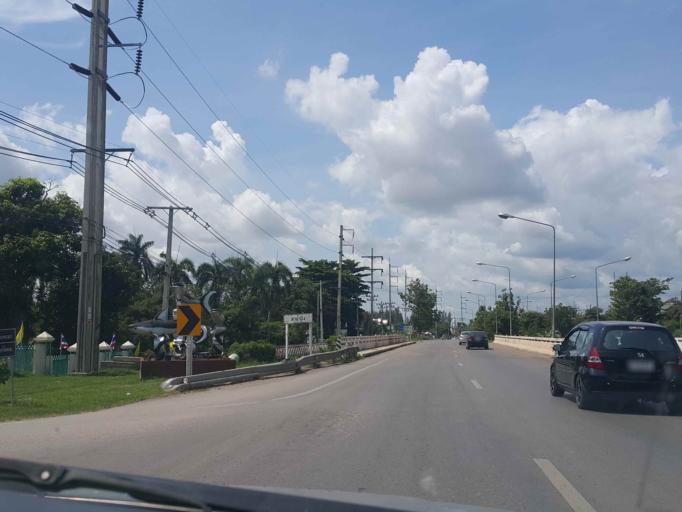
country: TH
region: Phayao
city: Phayao
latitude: 19.1605
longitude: 99.9143
